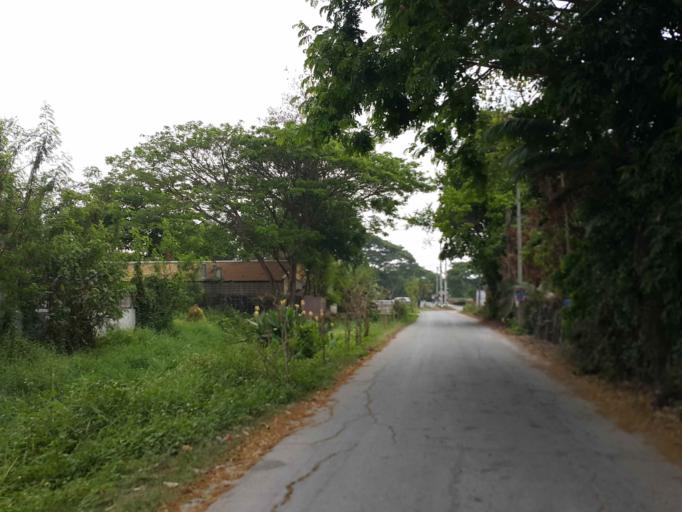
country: TH
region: Chiang Mai
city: Saraphi
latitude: 18.7494
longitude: 99.0206
